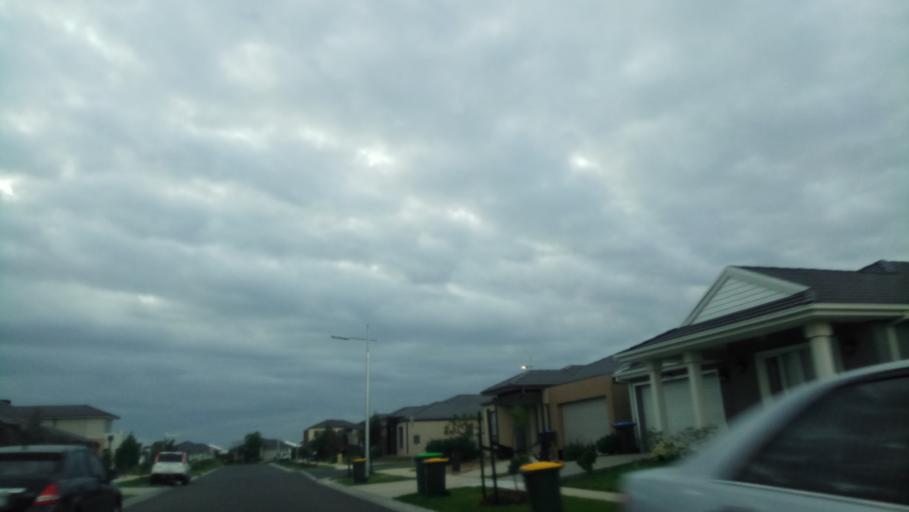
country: AU
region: Victoria
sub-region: Wyndham
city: Point Cook
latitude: -37.9137
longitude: 144.7598
